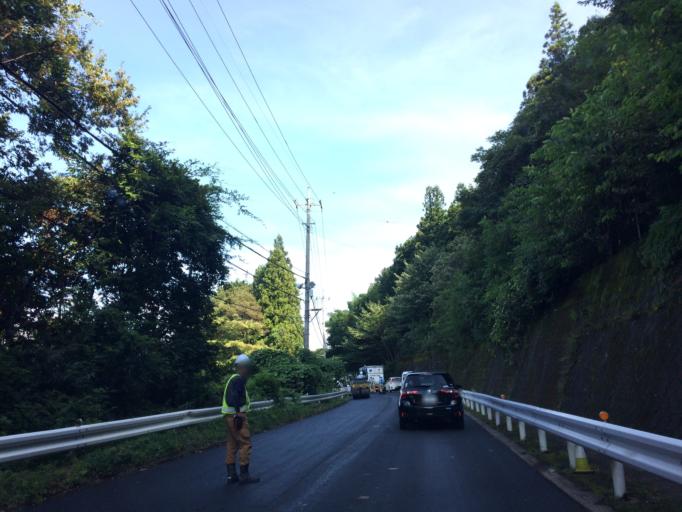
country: JP
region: Gunma
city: Nakanojomachi
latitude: 36.5491
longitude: 138.9129
